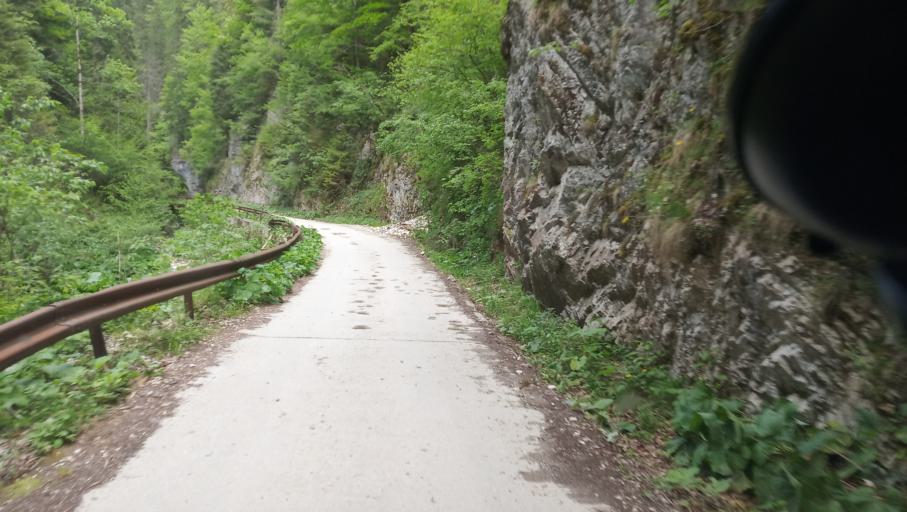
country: RO
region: Alba
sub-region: Comuna Scarisoara
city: Scarisoara
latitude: 46.4709
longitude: 22.8461
